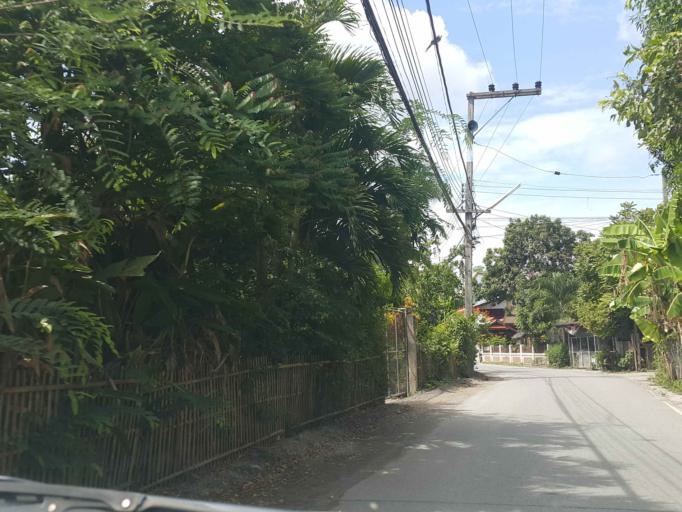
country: TH
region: Chiang Mai
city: Saraphi
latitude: 18.7328
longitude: 99.0499
